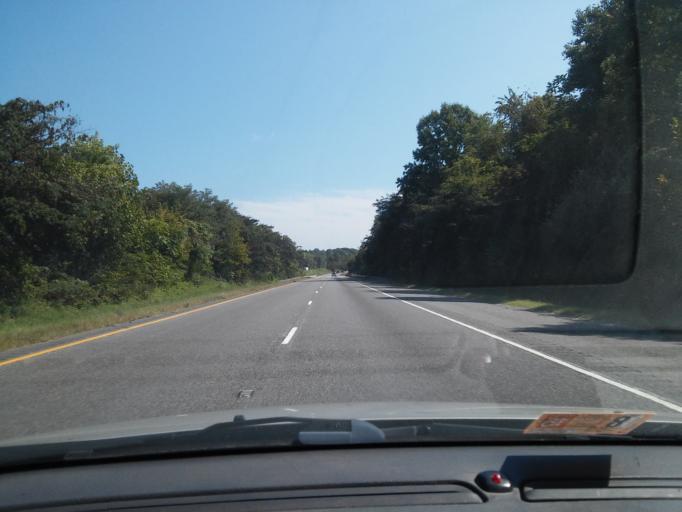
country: US
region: Virginia
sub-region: City of Charlottesville
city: Charlottesville
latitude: 38.0196
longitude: -78.4331
